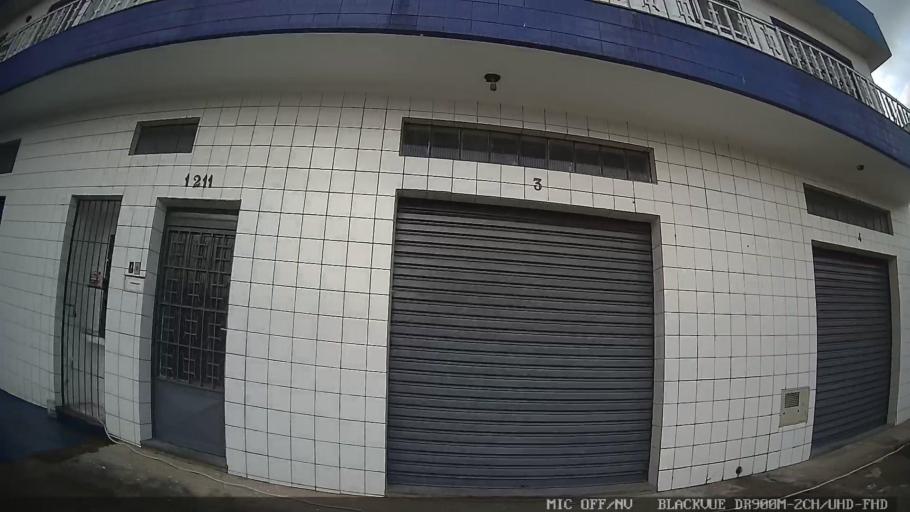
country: BR
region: Sao Paulo
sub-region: Itanhaem
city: Itanhaem
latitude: -24.1978
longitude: -46.8383
